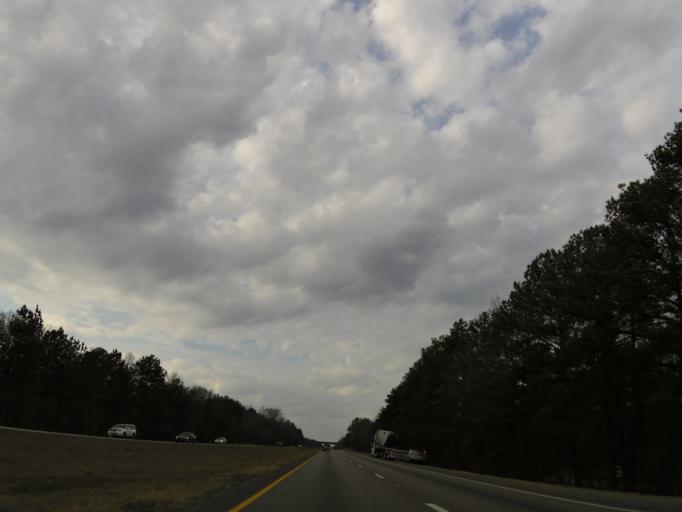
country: US
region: South Carolina
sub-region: Lexington County
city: Irmo
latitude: 34.1188
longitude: -81.1952
